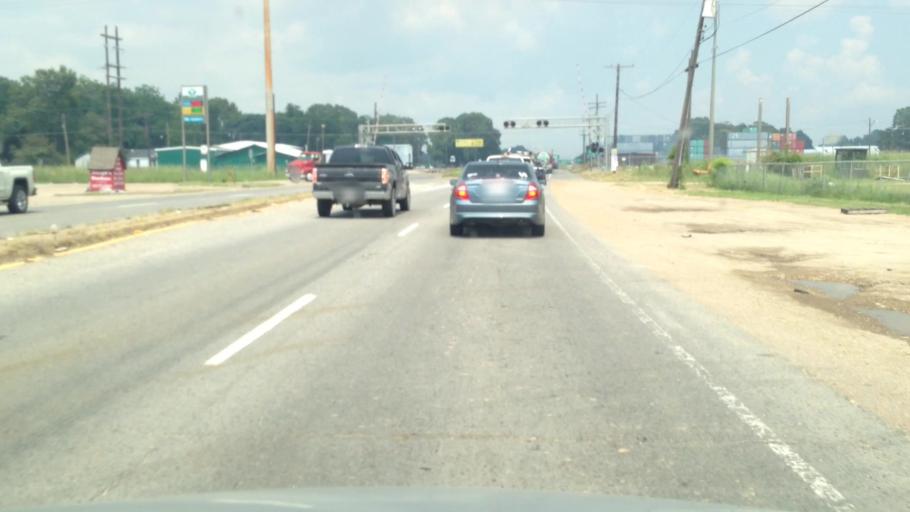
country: US
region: Louisiana
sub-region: East Baton Rouge Parish
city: Baton Rouge
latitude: 30.5082
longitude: -91.1789
